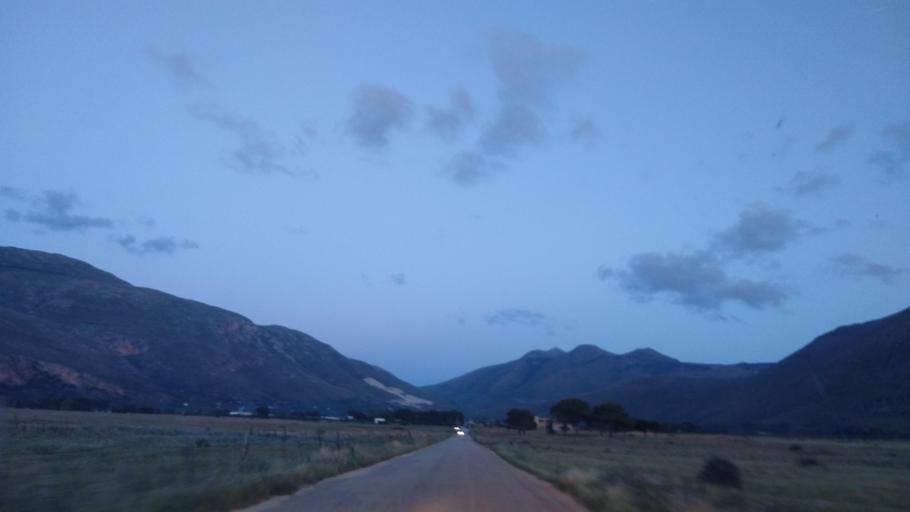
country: IT
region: Sicily
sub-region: Trapani
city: Castelluzzo
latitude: 38.1136
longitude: 12.7208
